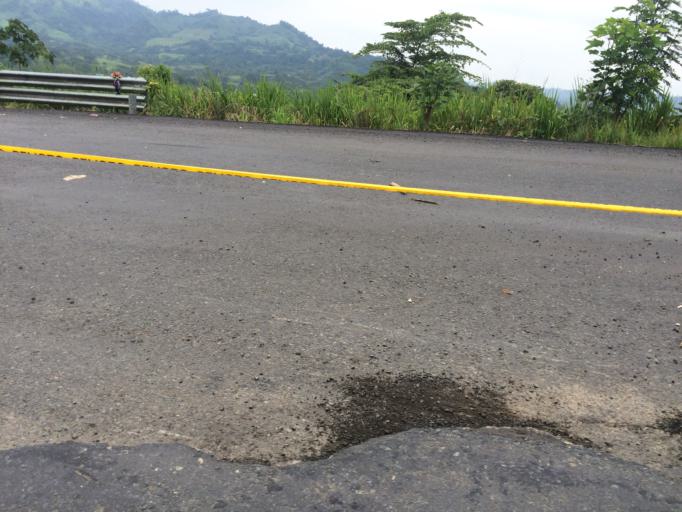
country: EC
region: Manabi
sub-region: Canton El Carmen
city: Wilfrido Loor Moreira
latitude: -0.3457
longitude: -79.7759
